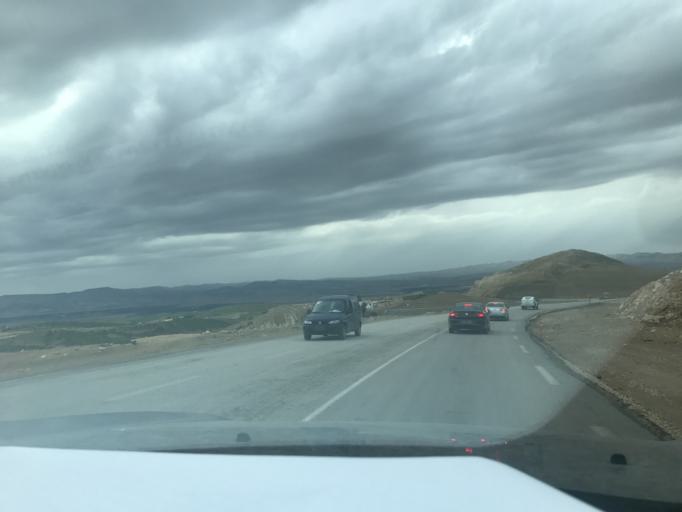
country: TN
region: Silyanah
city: Siliana
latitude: 36.0888
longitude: 9.4651
